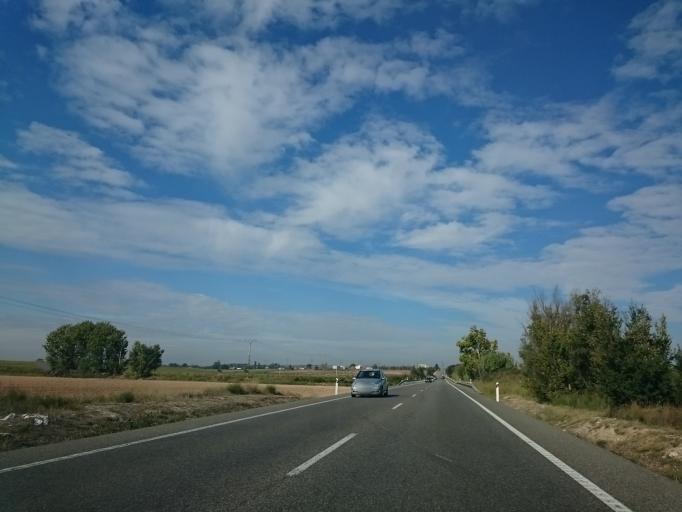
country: ES
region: Catalonia
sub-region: Provincia de Lleida
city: Alcoletge
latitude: 41.5982
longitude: 0.6980
